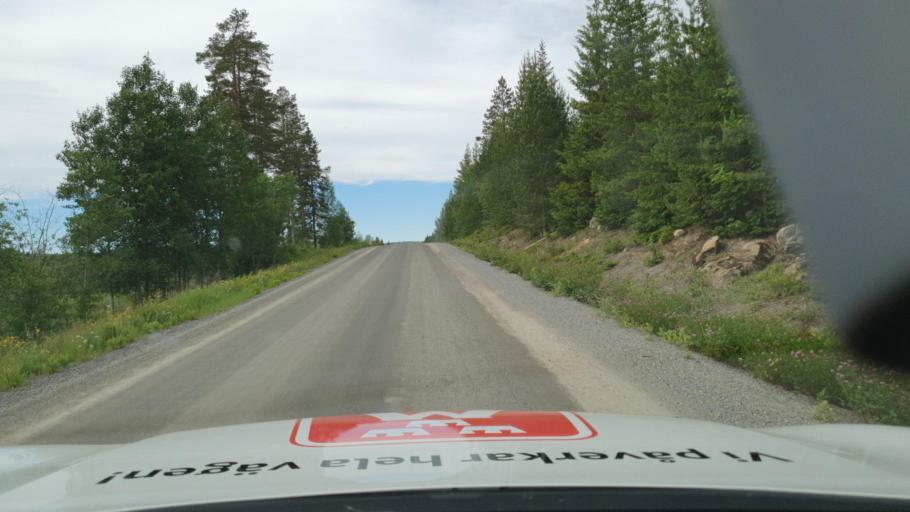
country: SE
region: Vaesterbotten
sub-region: Skelleftea Kommun
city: Burtraesk
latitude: 64.3707
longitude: 20.3795
